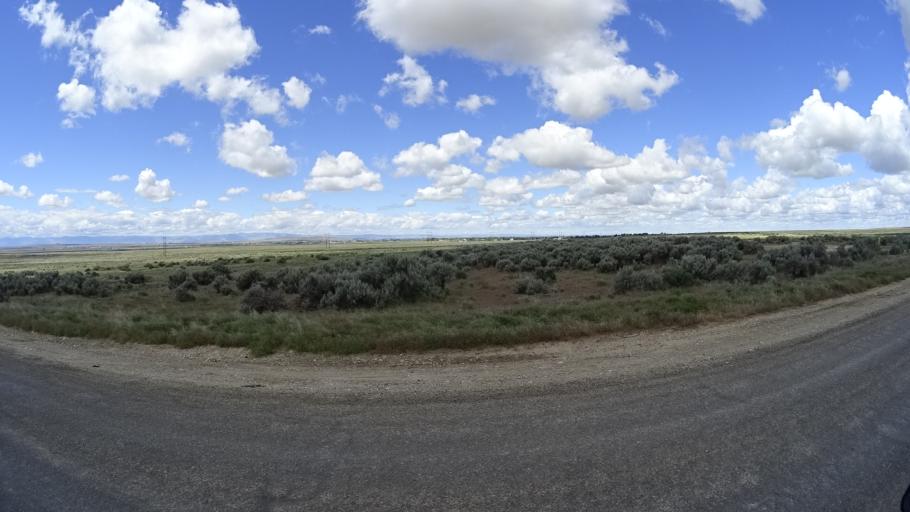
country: US
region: Idaho
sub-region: Ada County
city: Garden City
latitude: 43.4818
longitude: -116.2743
